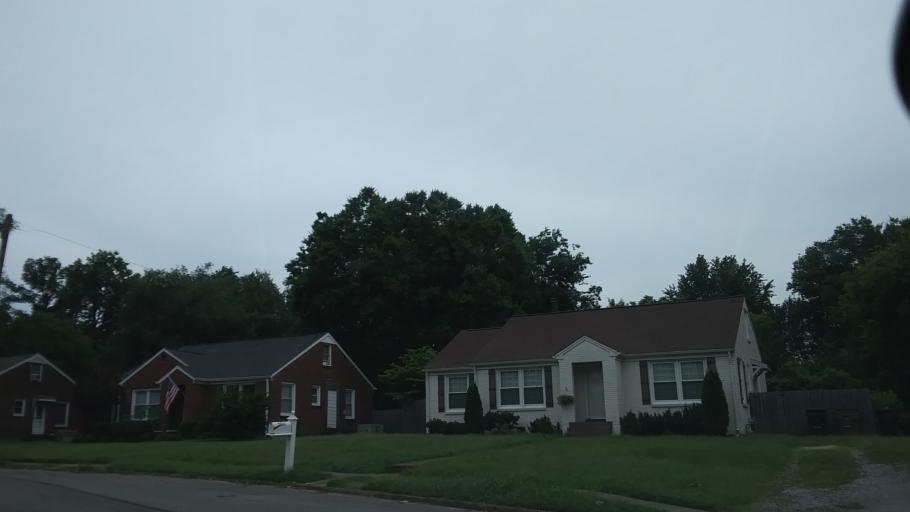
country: US
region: Tennessee
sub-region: Davidson County
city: Belle Meade
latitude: 36.1390
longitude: -86.8539
